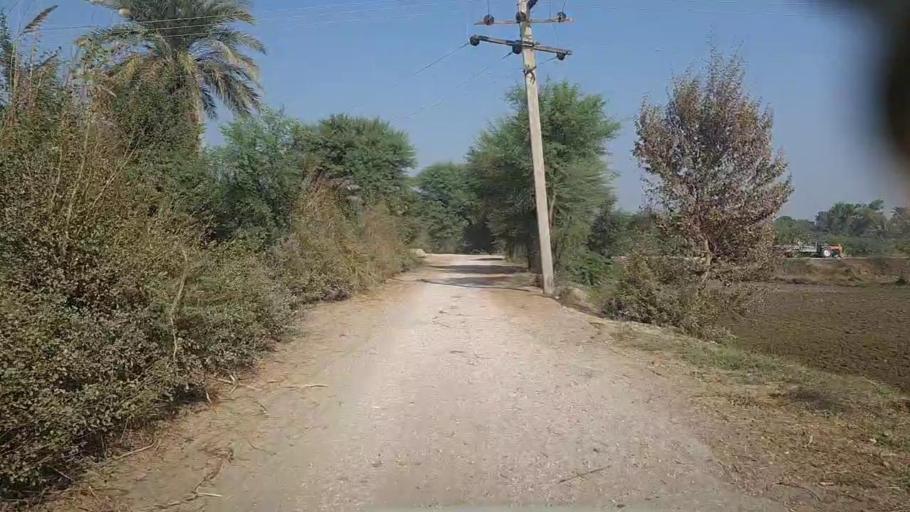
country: PK
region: Sindh
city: Karaundi
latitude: 26.9604
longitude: 68.4202
